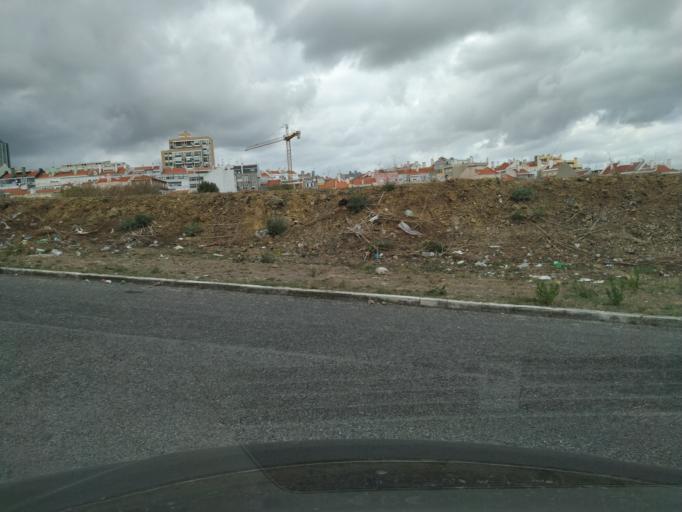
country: PT
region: Lisbon
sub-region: Lisbon
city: Lisbon
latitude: 38.7363
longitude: -9.1206
